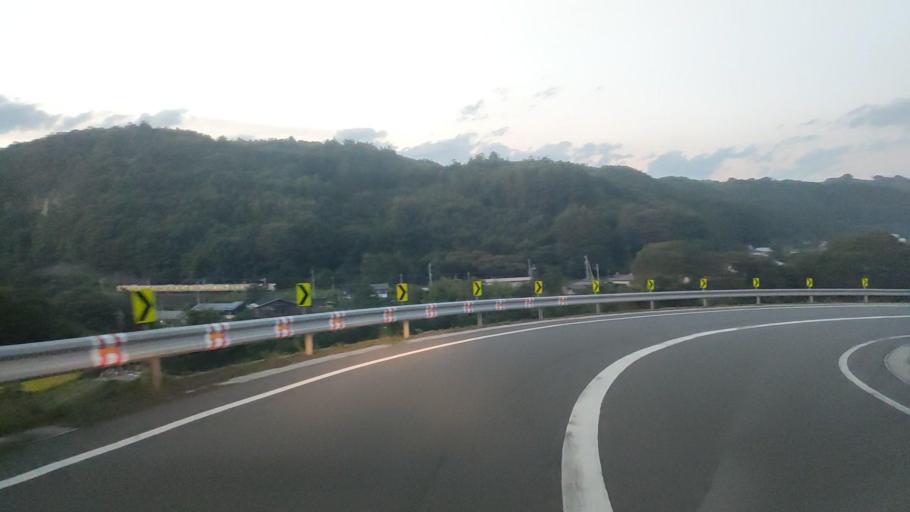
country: JP
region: Gunma
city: Nakanojomachi
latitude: 36.5455
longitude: 138.6002
